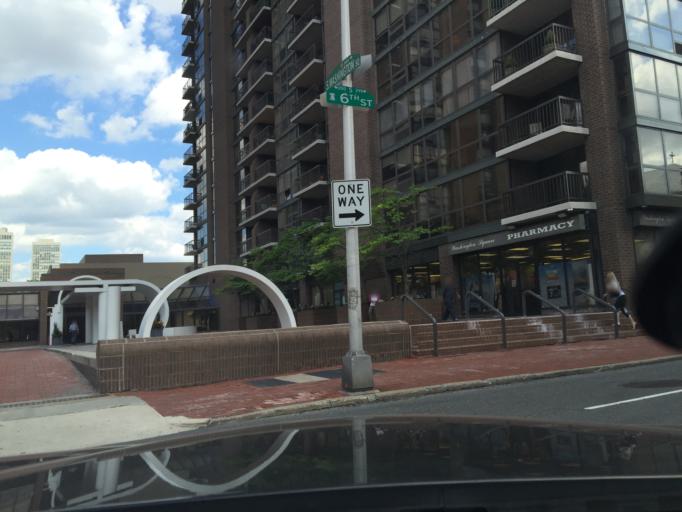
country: US
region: Pennsylvania
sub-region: Philadelphia County
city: Philadelphia
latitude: 39.9460
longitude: -75.1516
